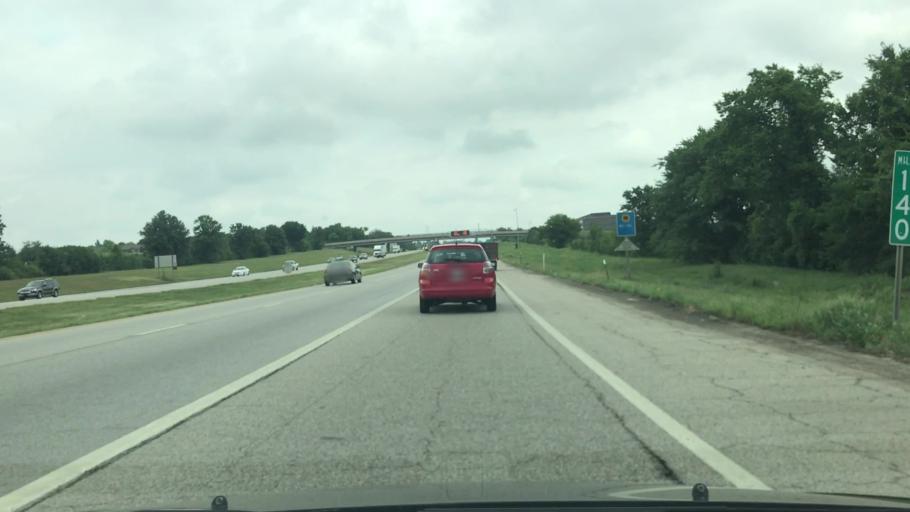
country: US
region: Kansas
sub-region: Johnson County
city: Lenexa
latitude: 38.8873
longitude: -94.6761
